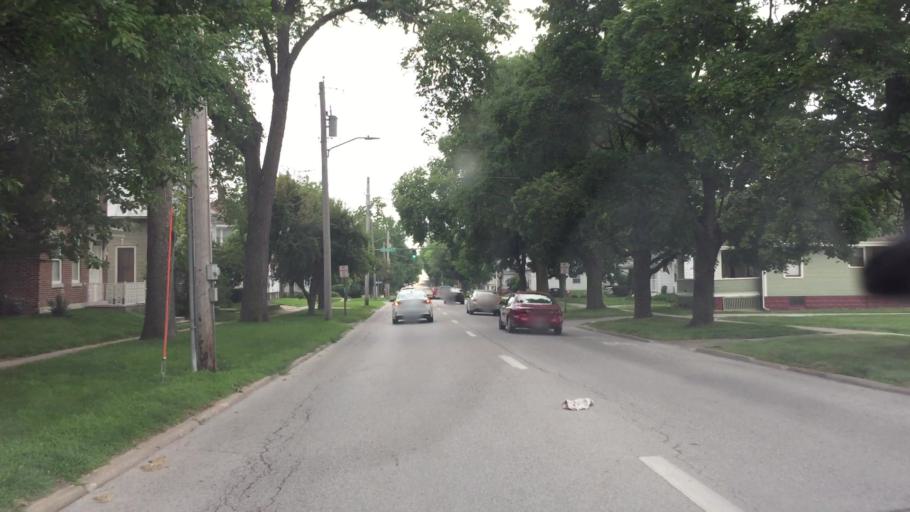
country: US
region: Iowa
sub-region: Johnson County
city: Iowa City
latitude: 41.6633
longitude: -91.5258
